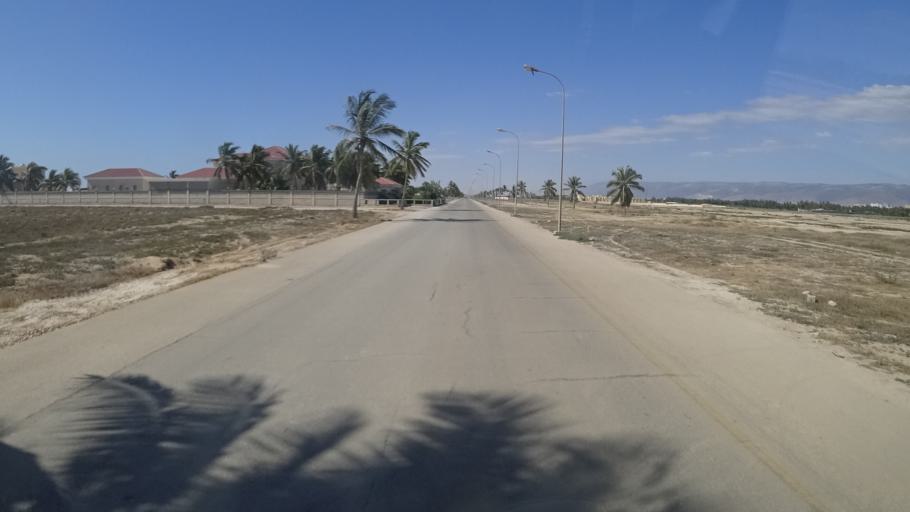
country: OM
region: Zufar
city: Salalah
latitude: 16.9950
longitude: 54.0578
